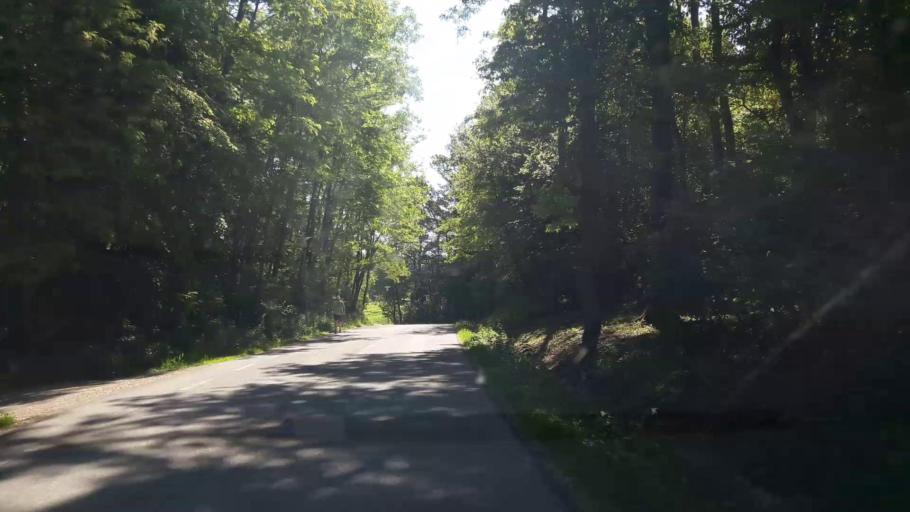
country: AT
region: Burgenland
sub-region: Politischer Bezirk Gussing
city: Stegersbach
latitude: 47.1707
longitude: 16.1421
